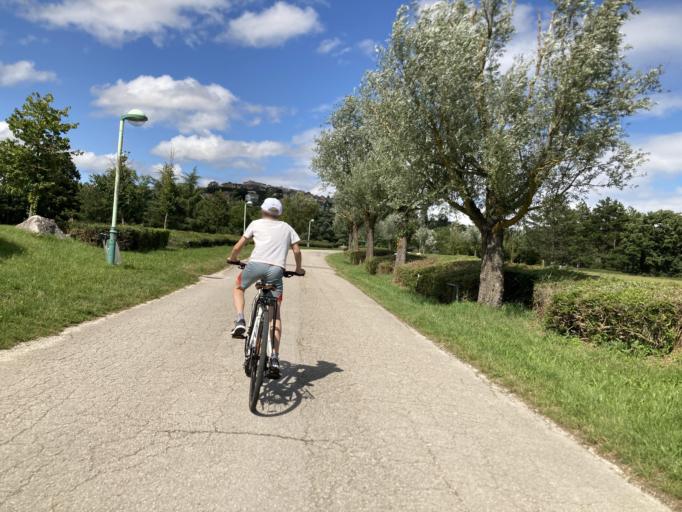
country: FR
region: Bourgogne
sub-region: Departement de la Cote-d'Or
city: Plombieres-les-Dijon
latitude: 47.3299
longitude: 4.9877
